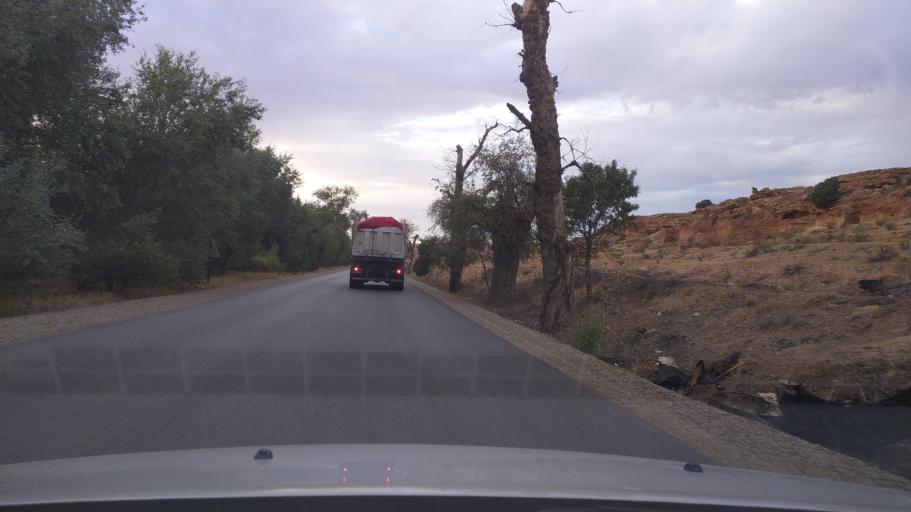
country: DZ
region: Tiaret
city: Frenda
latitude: 35.0489
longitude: 1.0789
